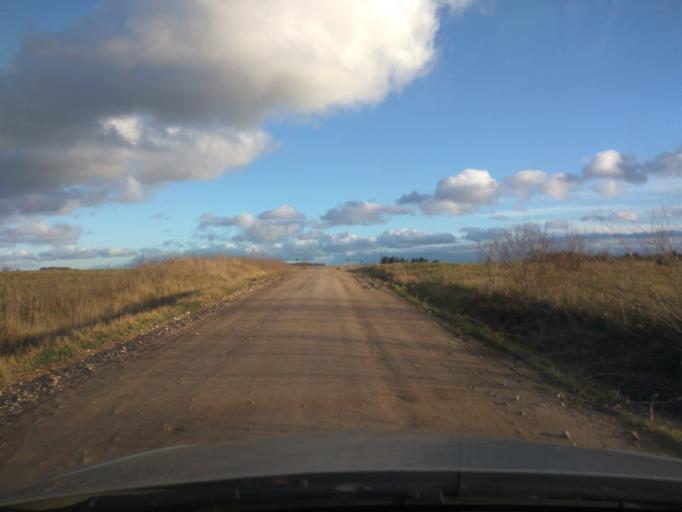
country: LV
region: Aizpute
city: Aizpute
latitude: 56.7482
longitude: 21.6094
